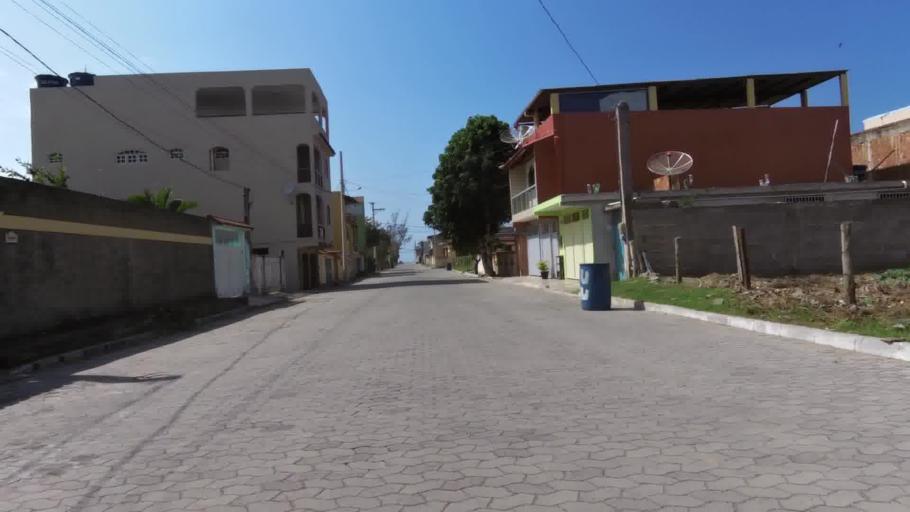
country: BR
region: Espirito Santo
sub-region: Marataizes
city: Marataizes
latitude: -21.0285
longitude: -40.8153
